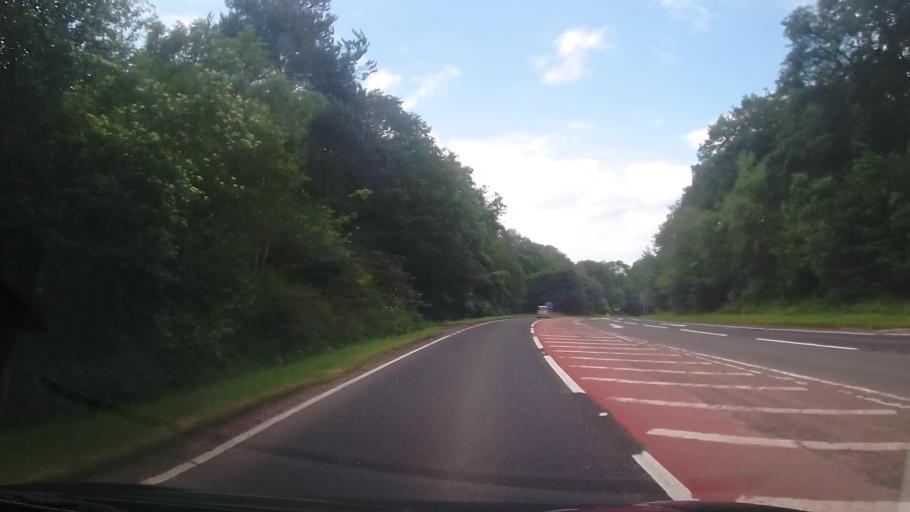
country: GB
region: England
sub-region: Herefordshire
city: Hope under Dinmore
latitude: 52.1600
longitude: -2.7222
